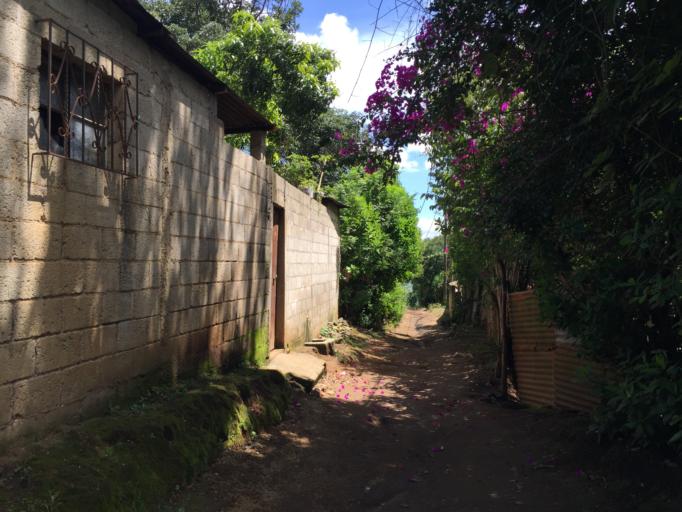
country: GT
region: Guatemala
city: Amatitlan
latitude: 14.5098
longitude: -90.6509
